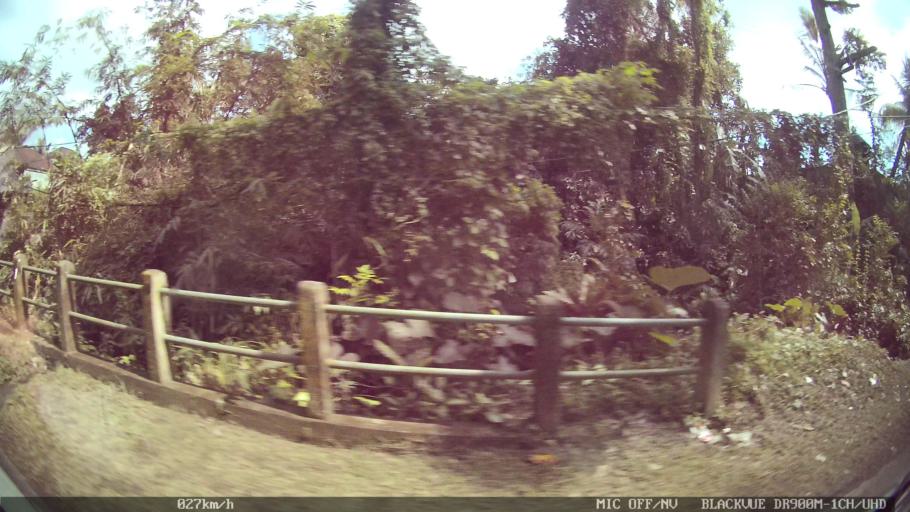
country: ID
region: Bali
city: Banjar Pesalakan
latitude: -8.5066
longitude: 115.3096
